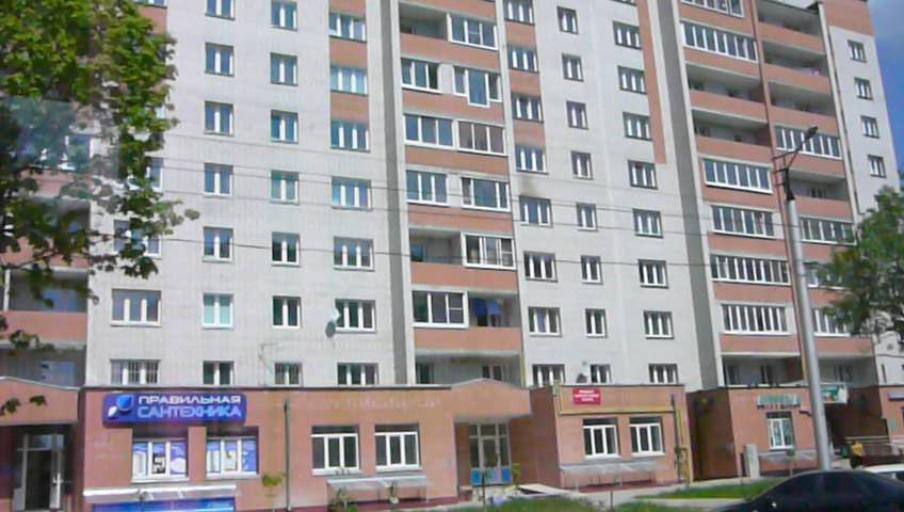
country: RU
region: Smolensk
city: Smolensk
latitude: 54.7682
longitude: 32.0035
